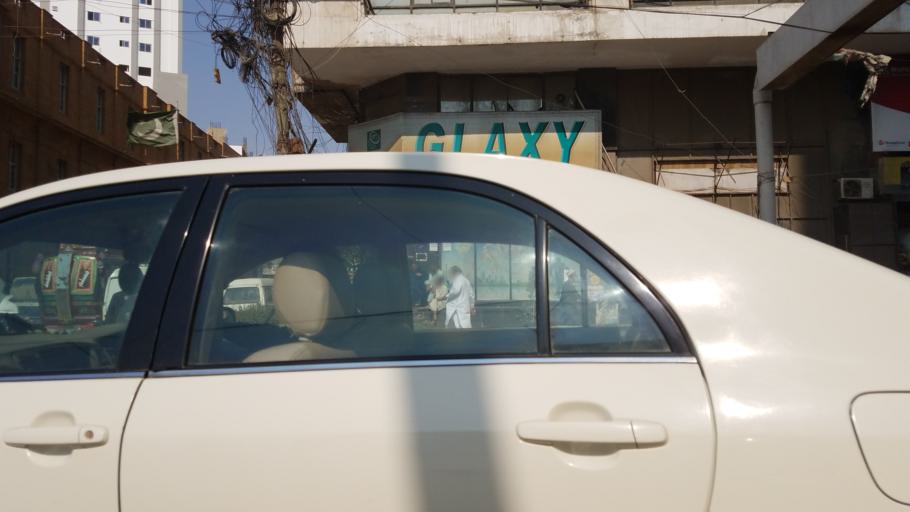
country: PK
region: Sindh
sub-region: Karachi District
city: Karachi
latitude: 24.8493
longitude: 67.0023
